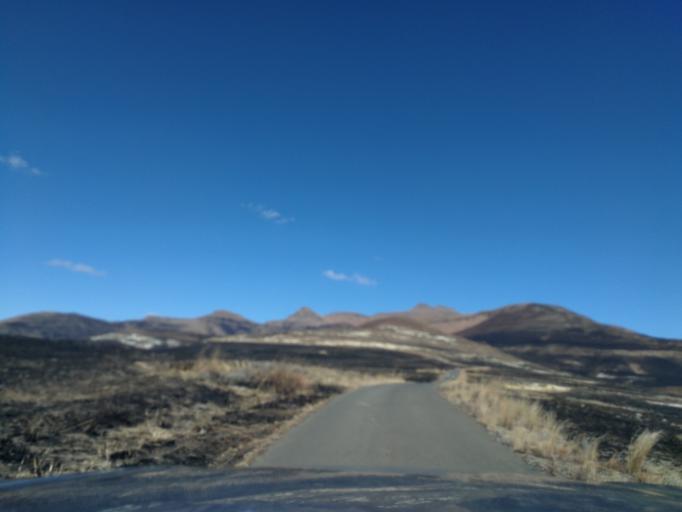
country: ZA
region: Orange Free State
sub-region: Thabo Mofutsanyana District Municipality
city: Phuthaditjhaba
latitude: -28.5160
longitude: 28.6223
